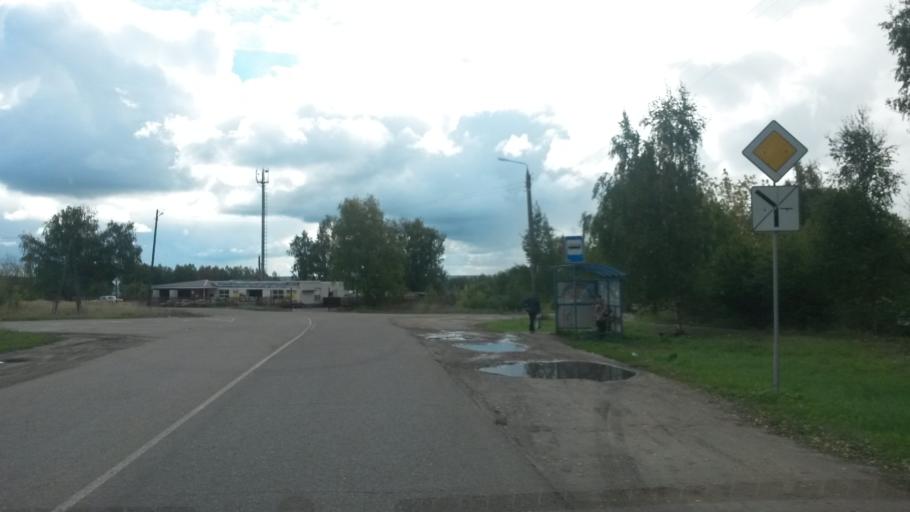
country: RU
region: Ivanovo
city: Zavolzhsk
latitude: 57.4669
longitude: 42.1629
